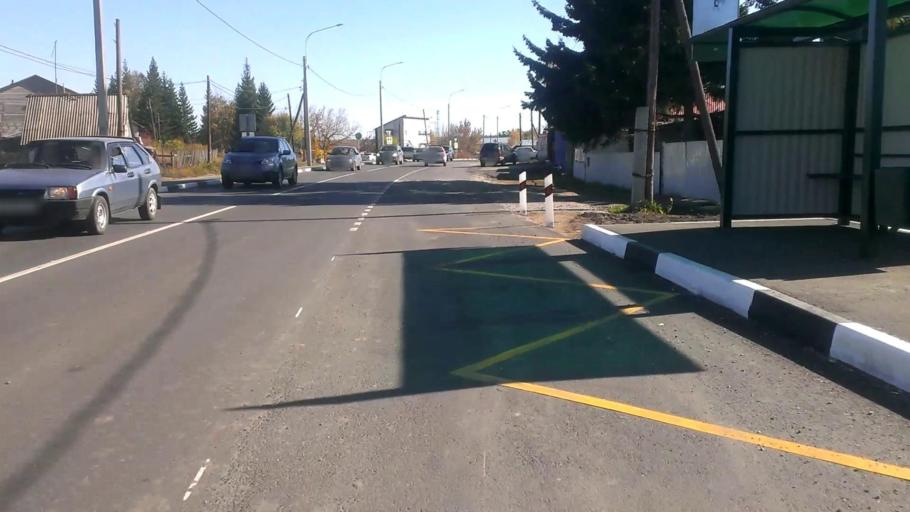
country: RU
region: Altai Krai
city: Sannikovo
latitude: 53.3168
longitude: 83.9566
